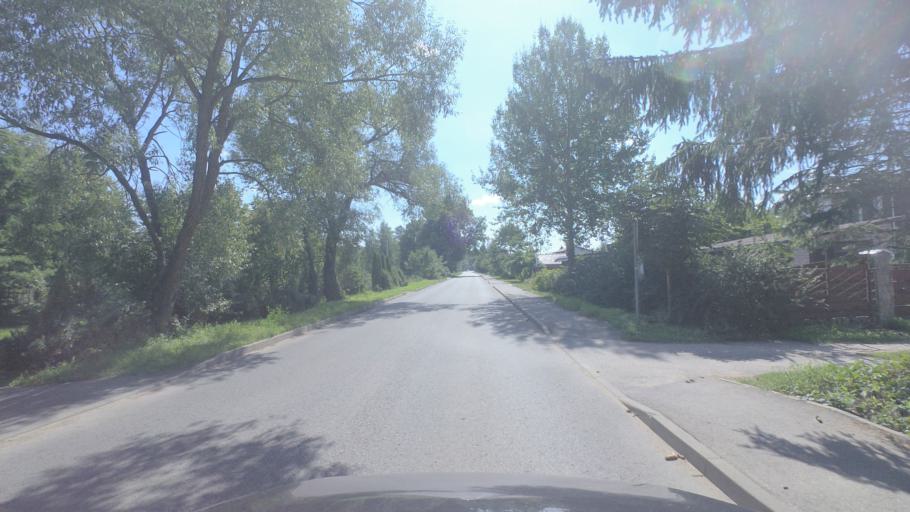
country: LT
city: Nemencine
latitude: 54.8397
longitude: 25.3709
